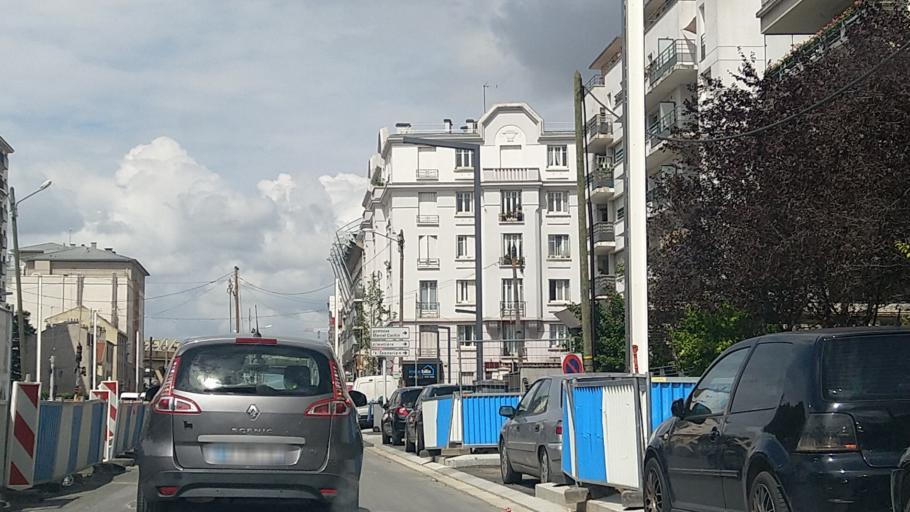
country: FR
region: Ile-de-France
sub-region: Departement du Val-de-Marne
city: Thiais
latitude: 48.7699
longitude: 2.4021
